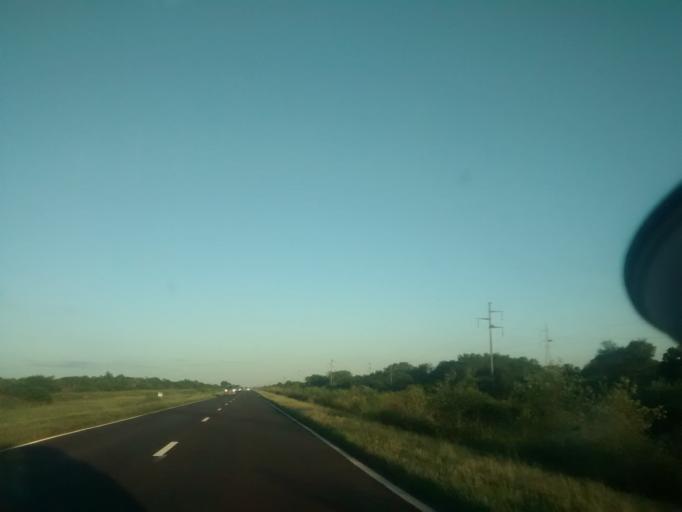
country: AR
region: Chaco
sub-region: Departamento de Presidencia de la Plaza
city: Presidencia de la Plaza
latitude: -27.0819
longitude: -59.6574
